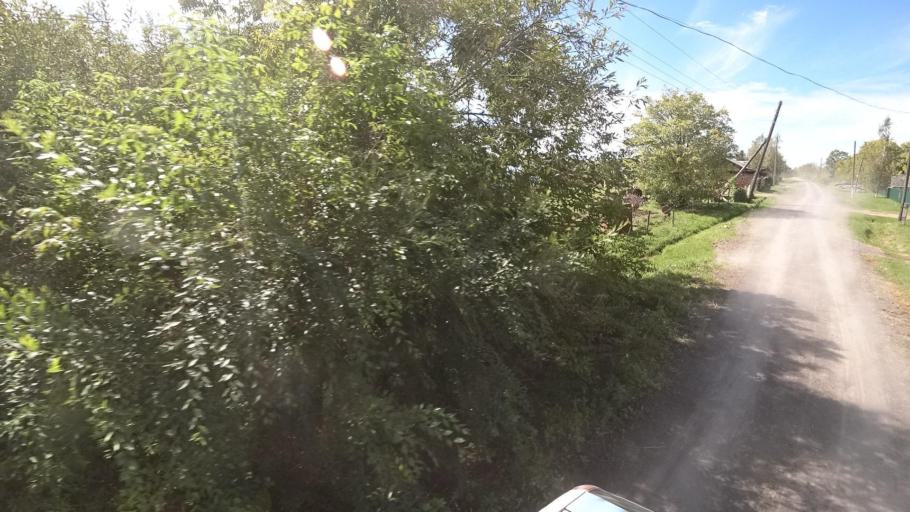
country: RU
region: Primorskiy
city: Yakovlevka
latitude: 44.4306
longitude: 133.5739
